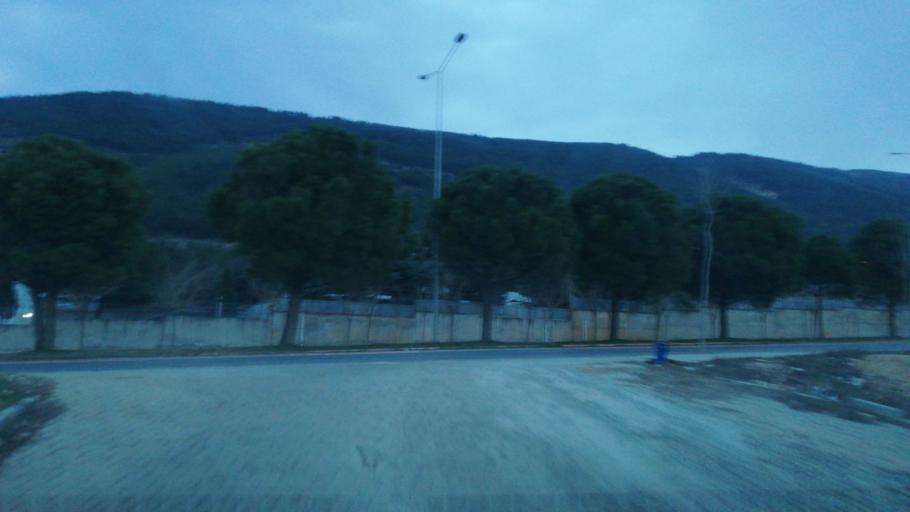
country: TR
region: Kahramanmaras
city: Kahramanmaras
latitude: 37.5997
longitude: 36.8337
